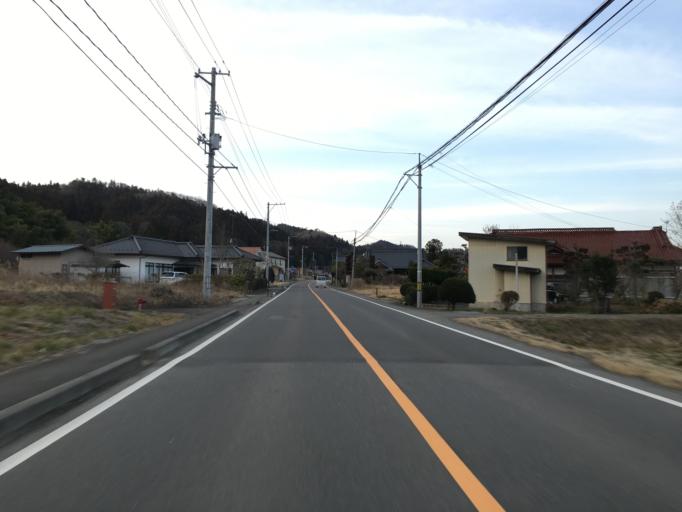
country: JP
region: Ibaraki
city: Daigo
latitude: 36.8977
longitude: 140.4089
